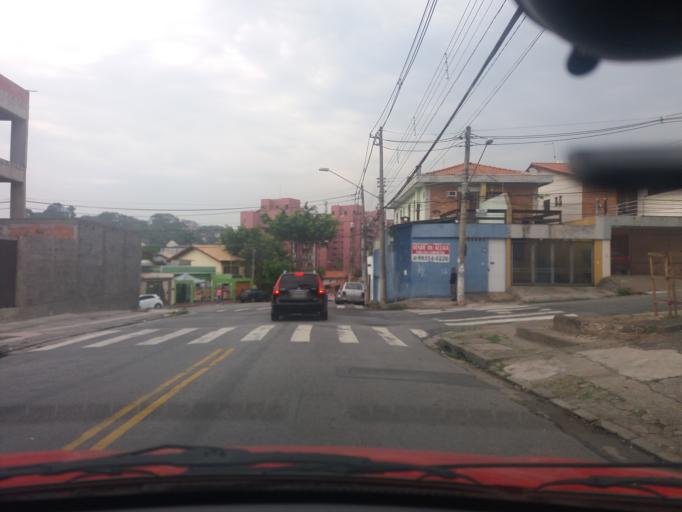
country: BR
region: Sao Paulo
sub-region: Taboao Da Serra
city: Taboao da Serra
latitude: -23.6023
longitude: -46.7273
